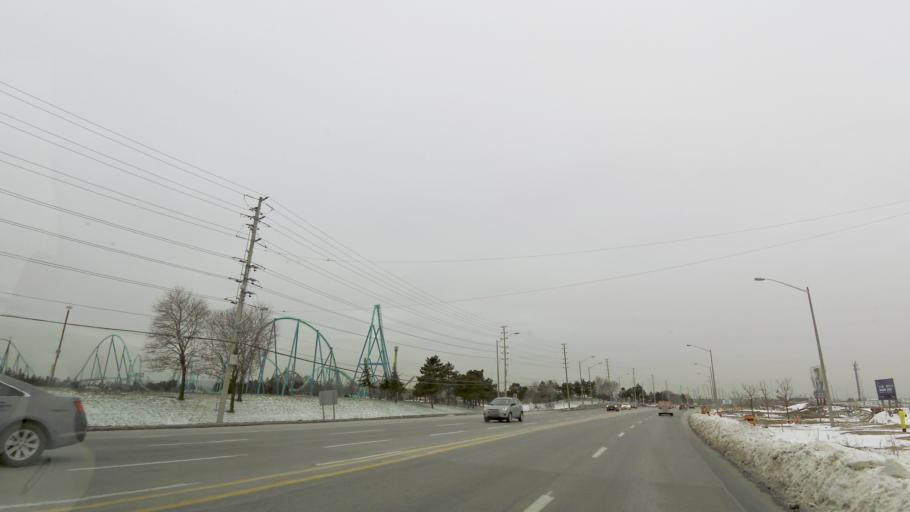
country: CA
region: Ontario
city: Vaughan
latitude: 43.8491
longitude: -79.5384
